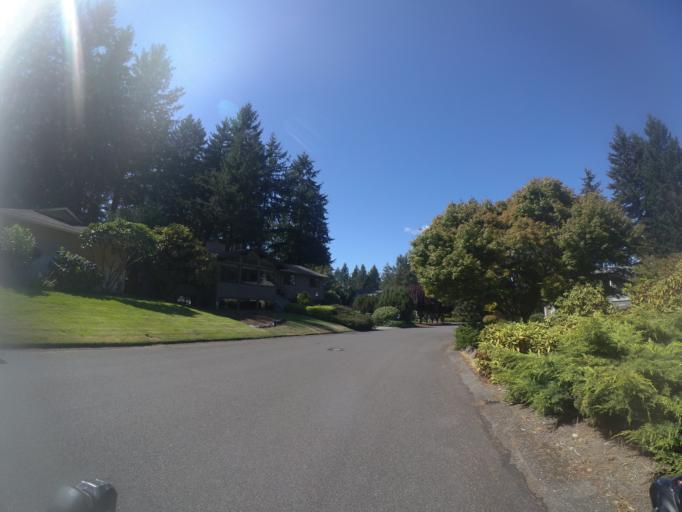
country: US
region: Washington
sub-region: Pierce County
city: University Place
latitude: 47.2140
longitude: -122.5594
